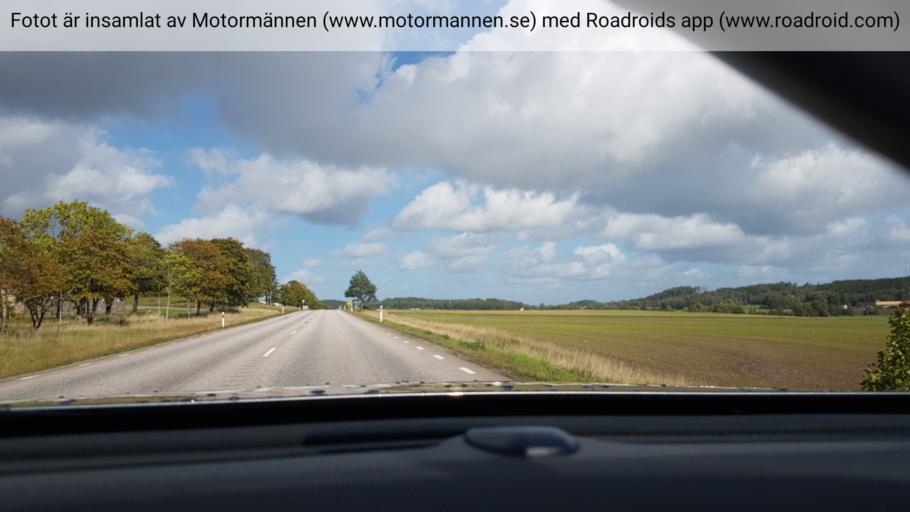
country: SE
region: Vaestra Goetaland
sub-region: Alingsas Kommun
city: Sollebrunn
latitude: 58.0891
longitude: 12.4966
